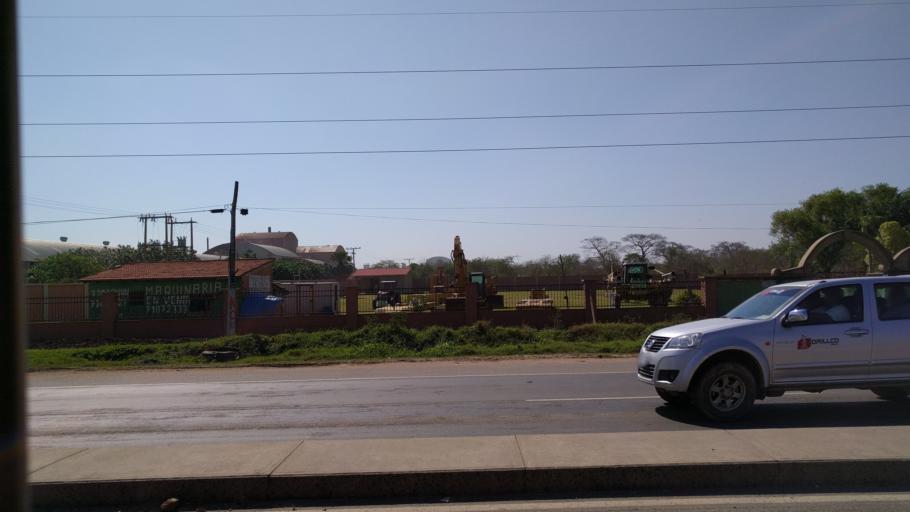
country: BO
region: Santa Cruz
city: Cotoca
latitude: -17.7609
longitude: -63.0201
